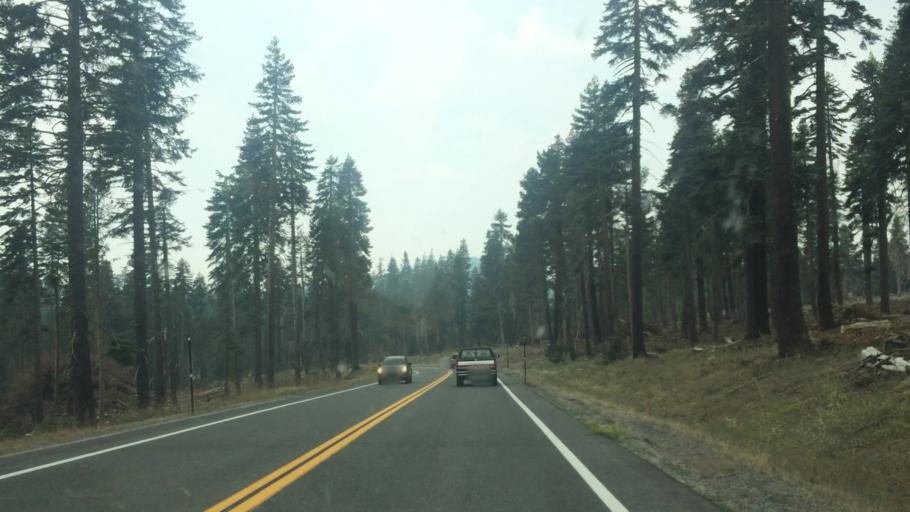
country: US
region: California
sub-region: El Dorado County
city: South Lake Tahoe
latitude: 38.6283
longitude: -120.2105
